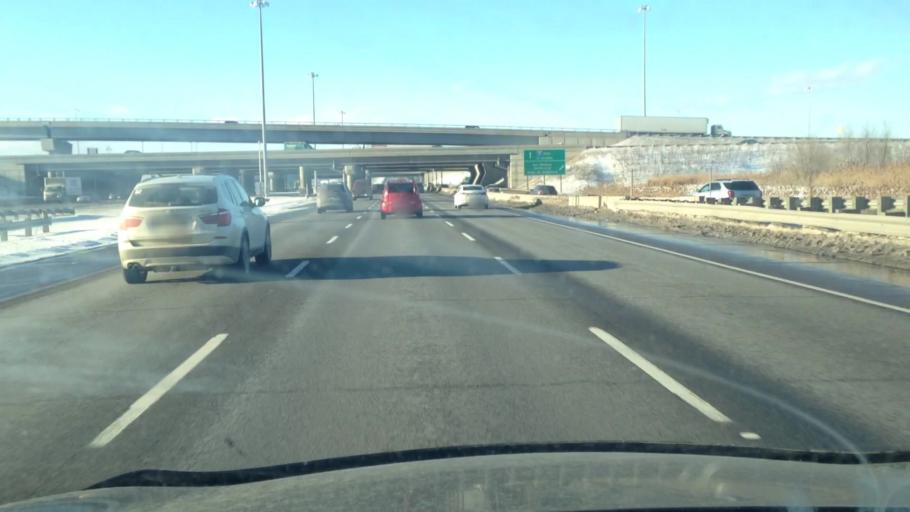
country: CA
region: Quebec
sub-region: Laurentides
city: Boisbriand
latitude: 45.6260
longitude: -73.8382
